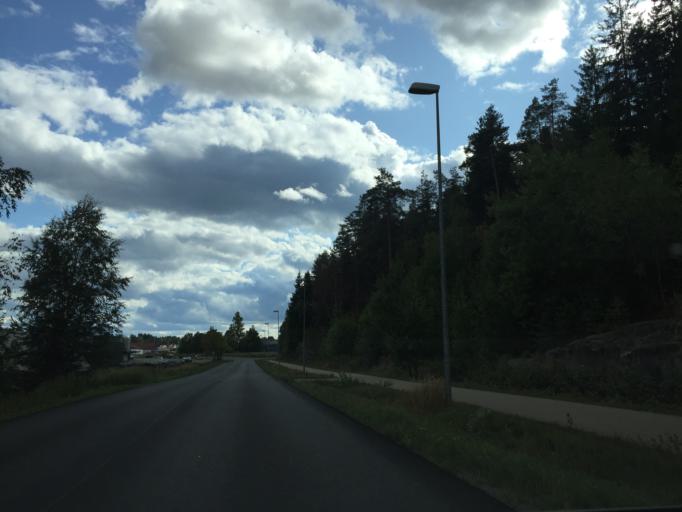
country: NO
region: Ostfold
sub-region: Askim
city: Askim
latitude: 59.5886
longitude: 11.1344
